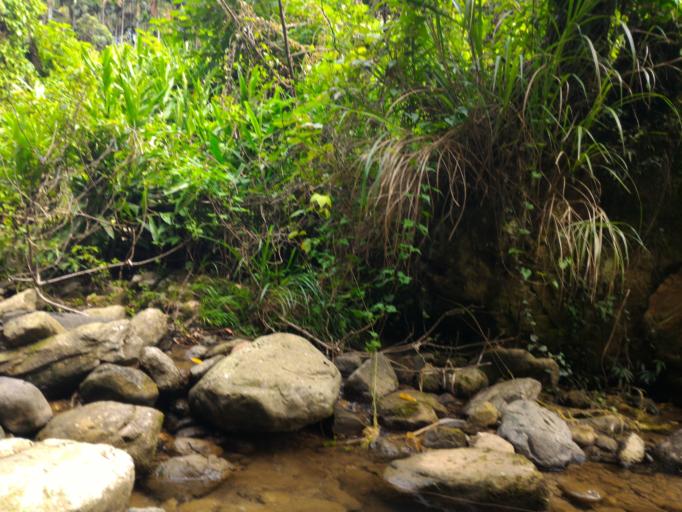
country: TW
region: Taipei
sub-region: Taipei
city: Banqiao
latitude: 24.9091
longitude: 121.4331
